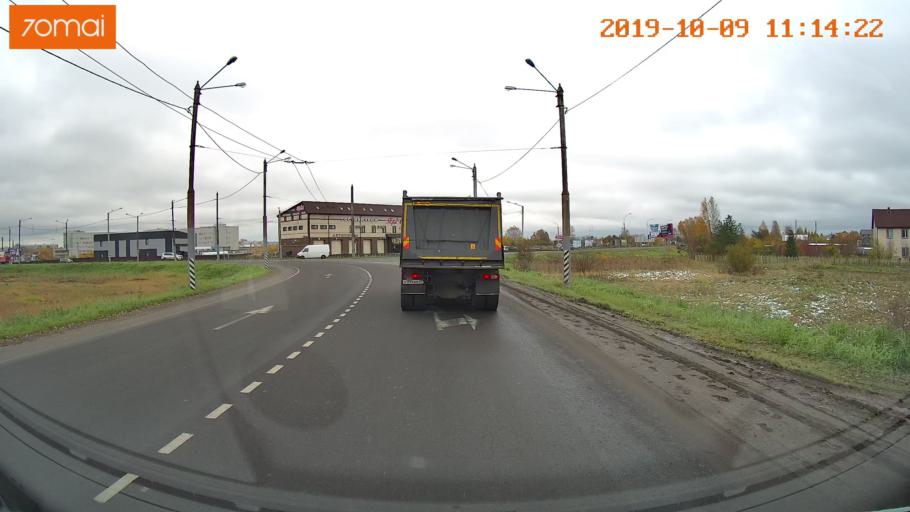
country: RU
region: Vologda
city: Vologda
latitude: 59.1867
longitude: 39.8521
